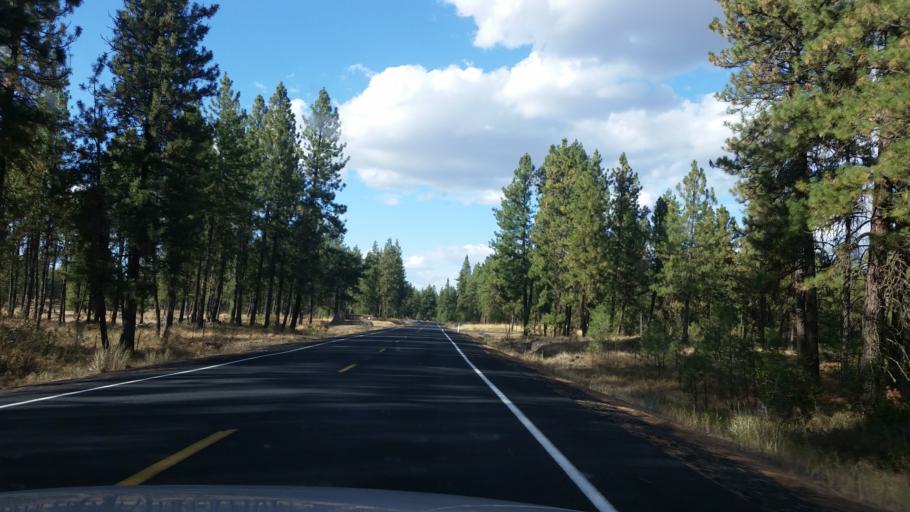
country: US
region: Washington
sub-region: Spokane County
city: Cheney
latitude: 47.4226
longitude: -117.5661
